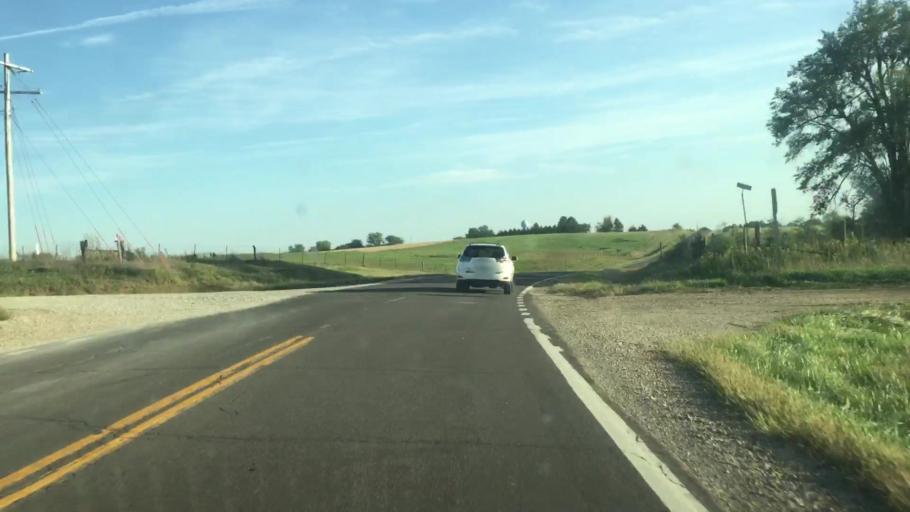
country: US
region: Kansas
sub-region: Brown County
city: Horton
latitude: 39.5658
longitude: -95.5247
